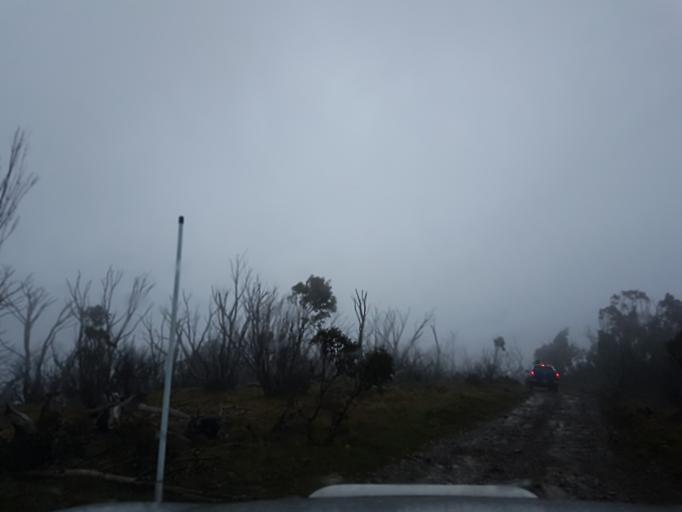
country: AU
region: Victoria
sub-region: Alpine
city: Mount Beauty
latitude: -37.0891
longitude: 147.0730
